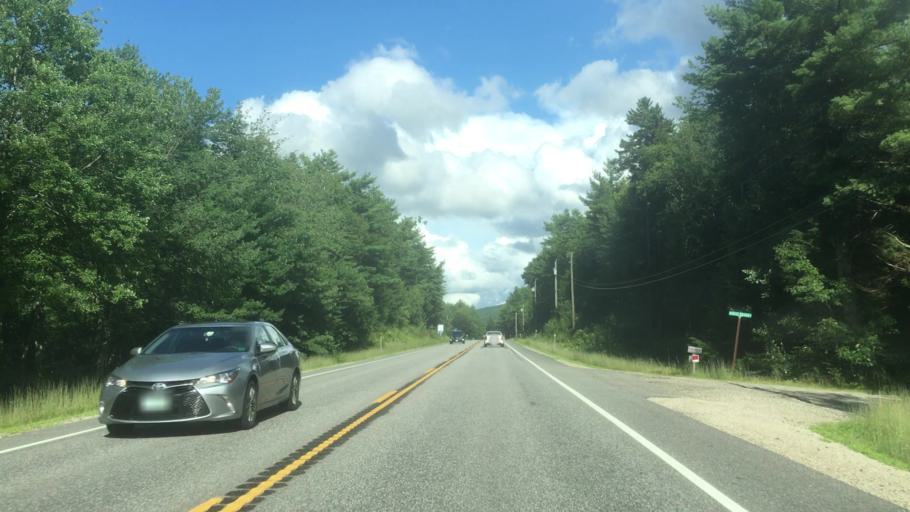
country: US
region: New Hampshire
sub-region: Cheshire County
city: Harrisville
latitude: 43.0371
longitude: -72.0923
